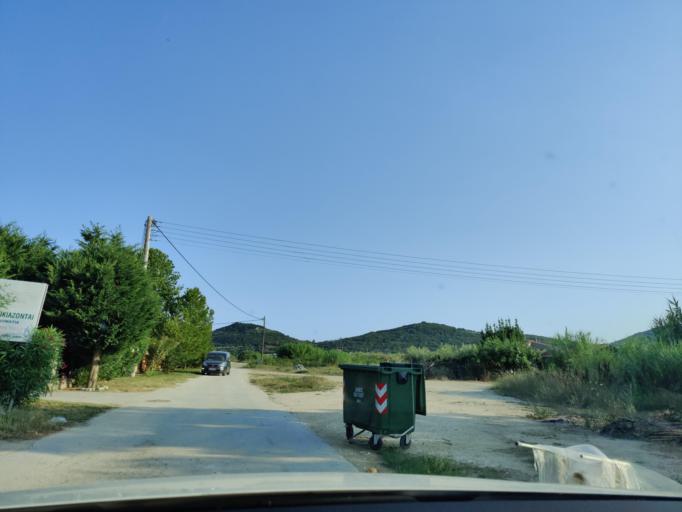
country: GR
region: East Macedonia and Thrace
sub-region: Nomos Kavalas
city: Nea Peramos
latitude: 40.8311
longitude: 24.3029
